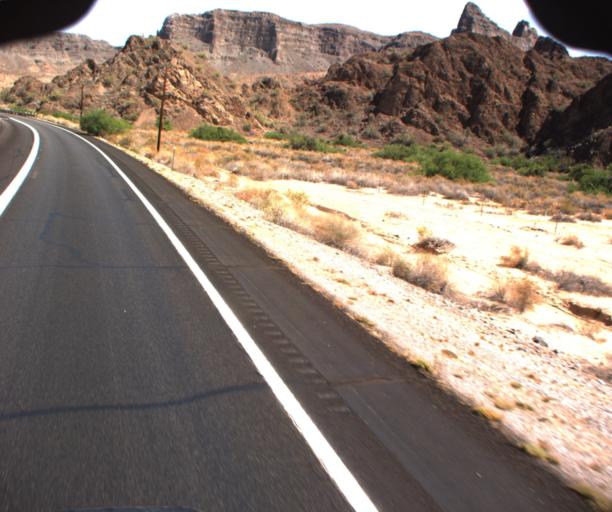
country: US
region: Arizona
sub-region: La Paz County
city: Cienega Springs
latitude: 34.2535
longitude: -114.1400
